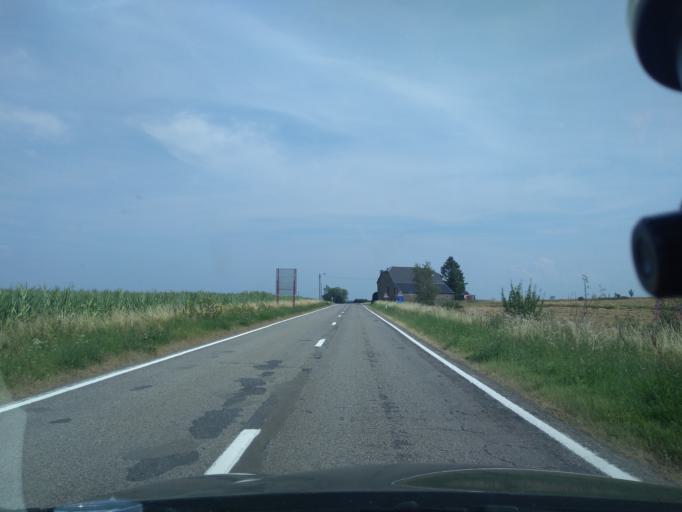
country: BE
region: Wallonia
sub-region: Province du Luxembourg
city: Bertogne
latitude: 50.1482
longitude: 5.7064
